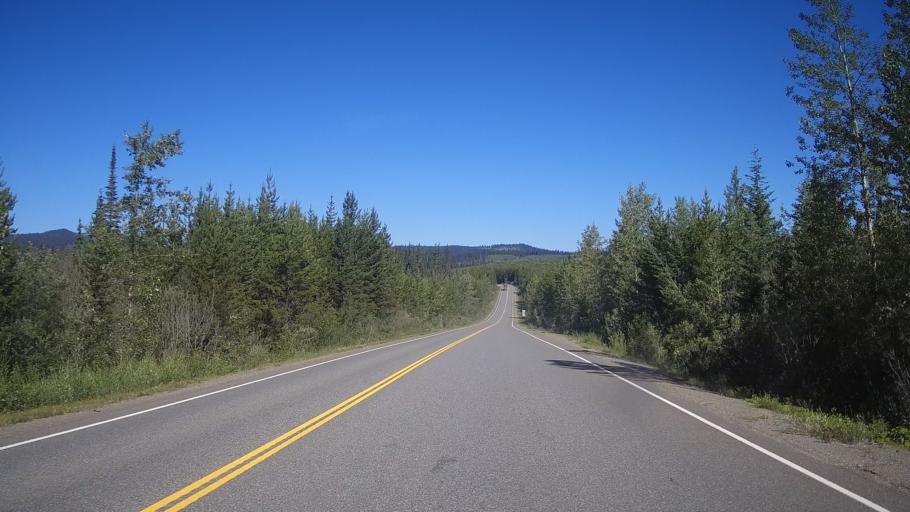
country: CA
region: British Columbia
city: Kamloops
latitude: 51.4985
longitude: -120.3422
